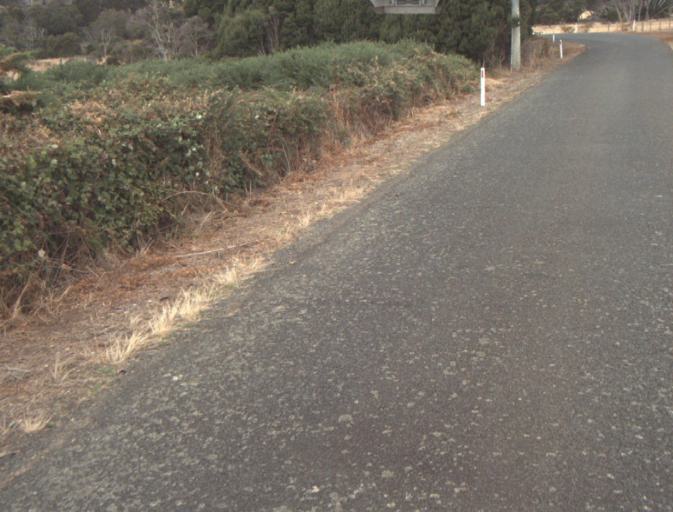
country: AU
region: Tasmania
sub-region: Launceston
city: Mayfield
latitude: -41.2836
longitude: 147.0113
